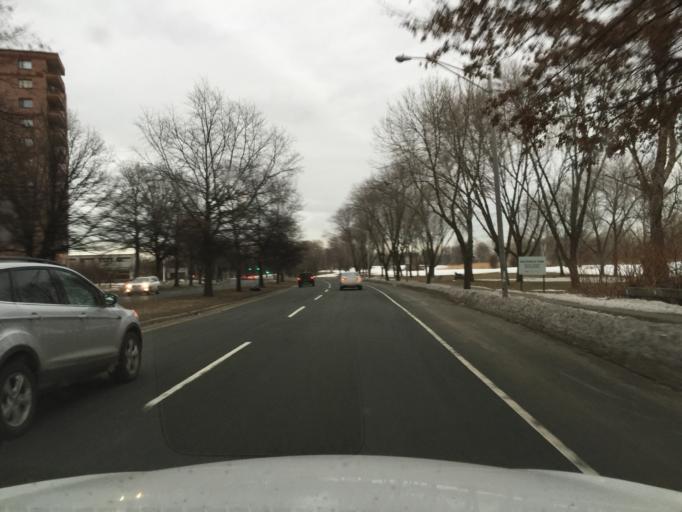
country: US
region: Massachusetts
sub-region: Middlesex County
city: Somerville
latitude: 42.4049
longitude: -71.0925
